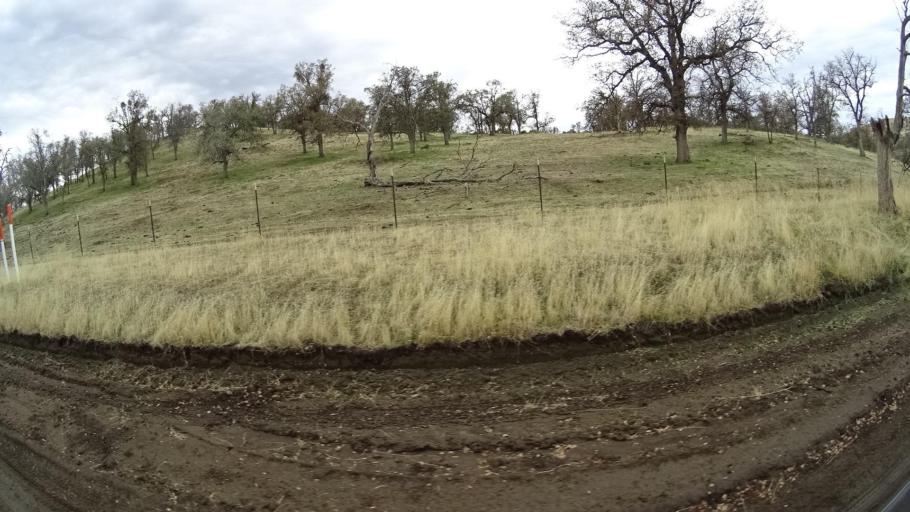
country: US
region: California
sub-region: Kern County
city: Stallion Springs
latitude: 35.1229
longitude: -118.7213
